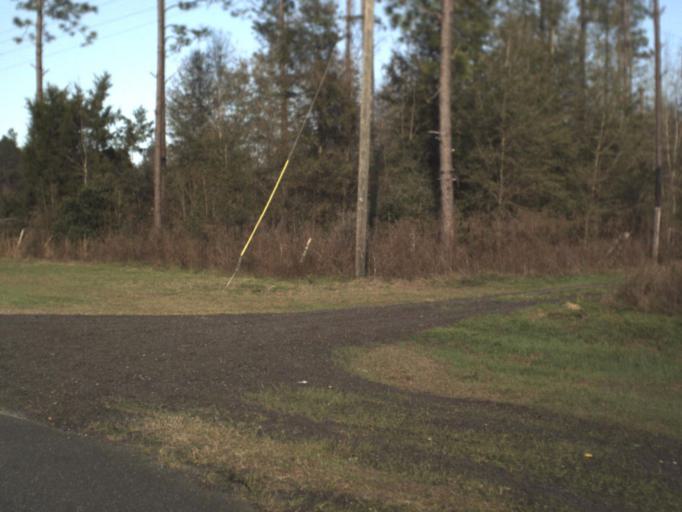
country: US
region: Florida
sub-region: Calhoun County
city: Blountstown
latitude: 30.5121
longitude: -85.1998
